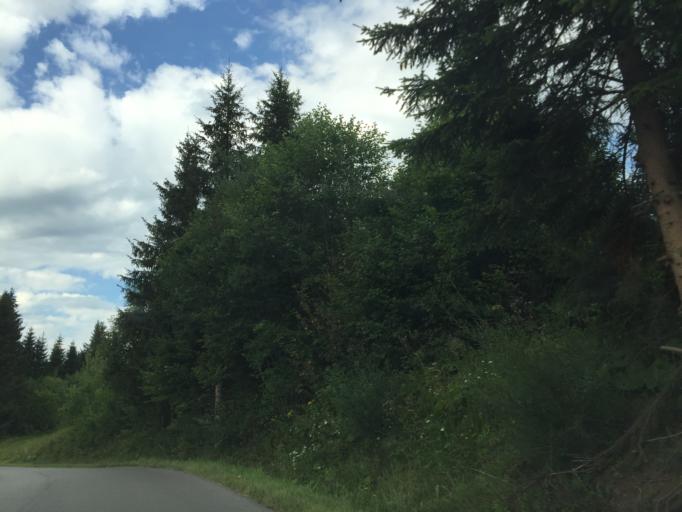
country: SK
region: Zilinsky
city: Namestovo
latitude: 49.4085
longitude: 19.3338
